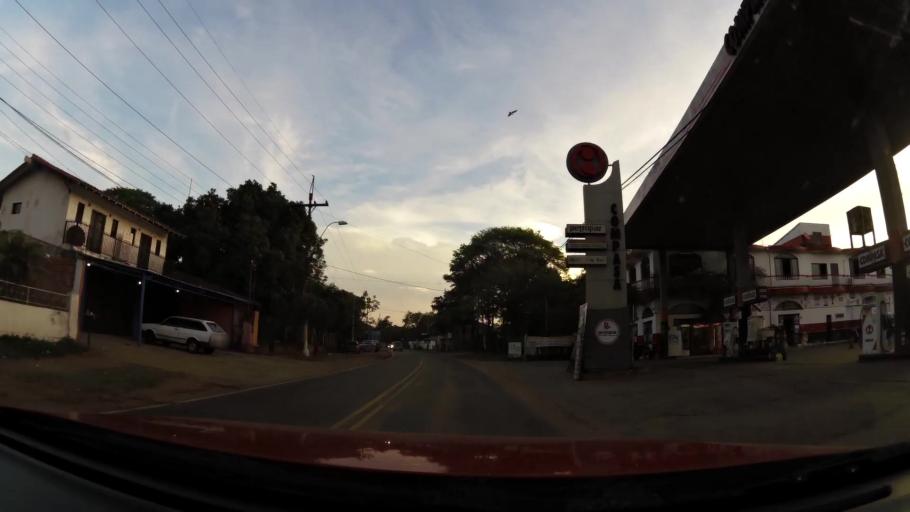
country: PY
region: Central
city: San Lorenzo
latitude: -25.3575
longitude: -57.4910
